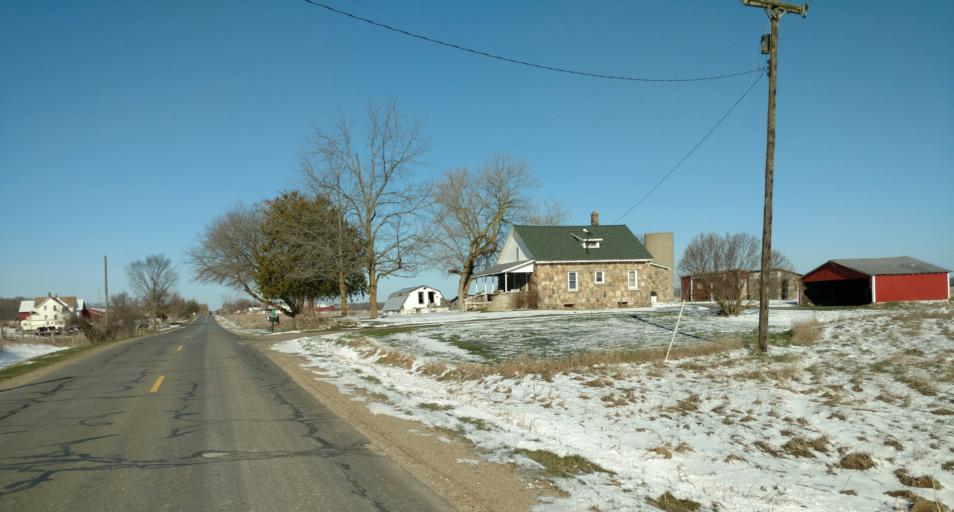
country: US
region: Michigan
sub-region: Gladwin County
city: Gladwin
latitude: 44.0307
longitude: -84.4474
